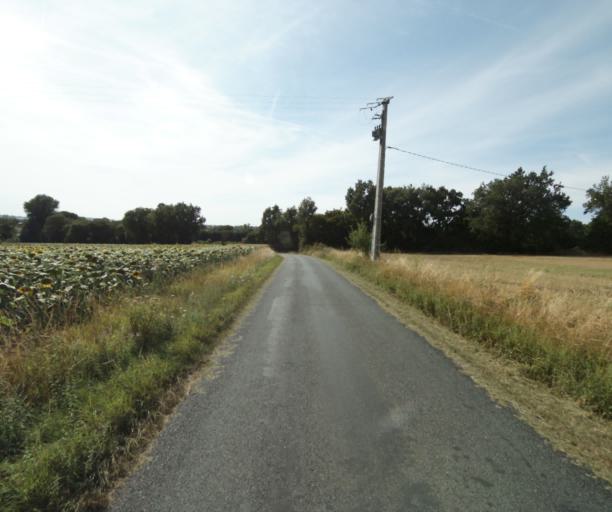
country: FR
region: Midi-Pyrenees
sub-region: Departement du Tarn
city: Puylaurens
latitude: 43.5260
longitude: 2.0504
